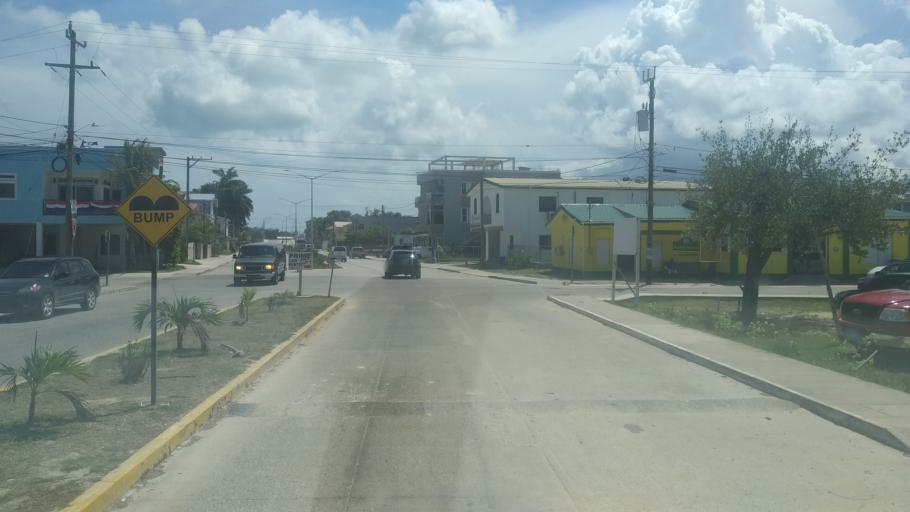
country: BZ
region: Belize
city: Belize City
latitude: 17.5109
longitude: -88.2215
